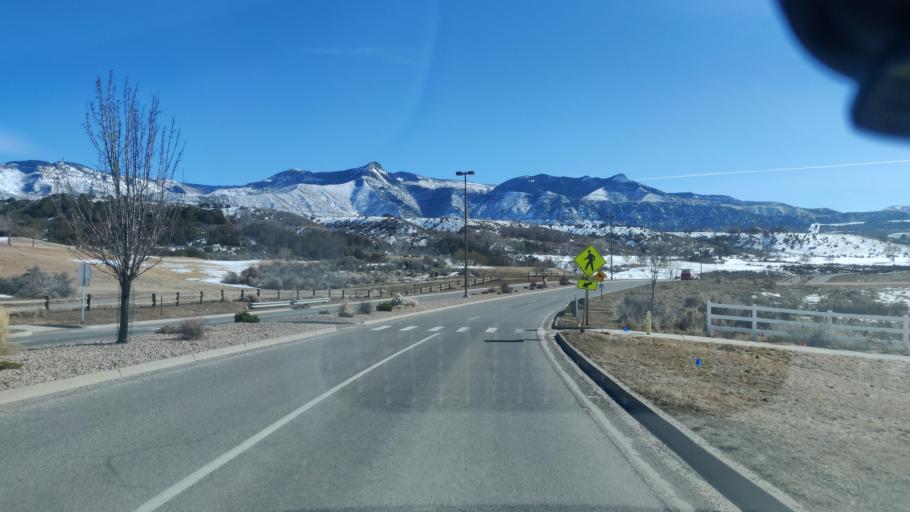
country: US
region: Colorado
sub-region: Garfield County
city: Battlement Mesa
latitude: 39.4536
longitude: -108.0332
